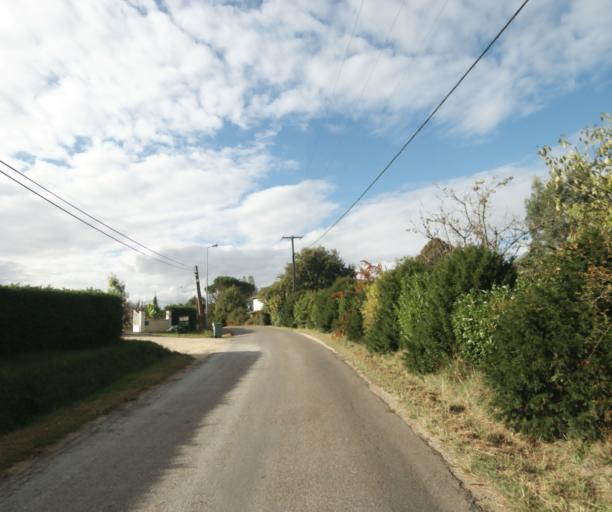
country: FR
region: Midi-Pyrenees
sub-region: Departement du Gers
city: Eauze
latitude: 43.8673
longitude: 0.0964
